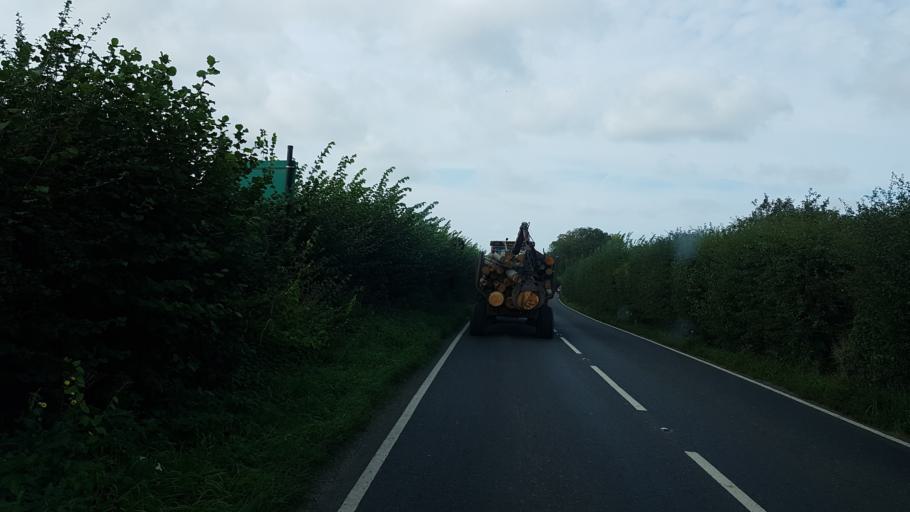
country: GB
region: England
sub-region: Kent
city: Maidstone
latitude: 51.2283
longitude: 0.5510
